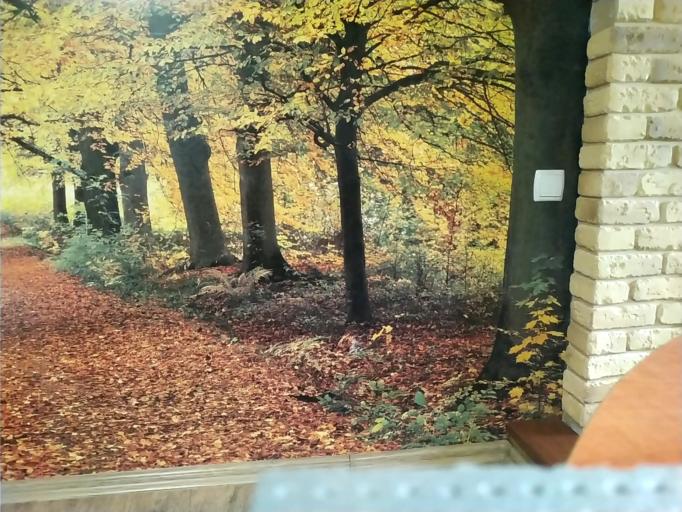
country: RU
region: Tverskaya
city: Staritsa
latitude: 56.5279
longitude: 35.0424
